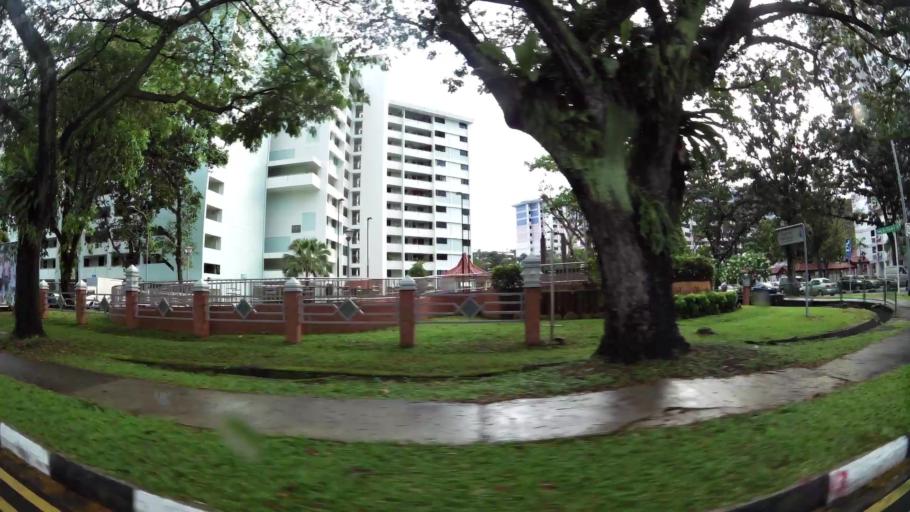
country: SG
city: Singapore
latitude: 1.3757
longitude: 103.8550
